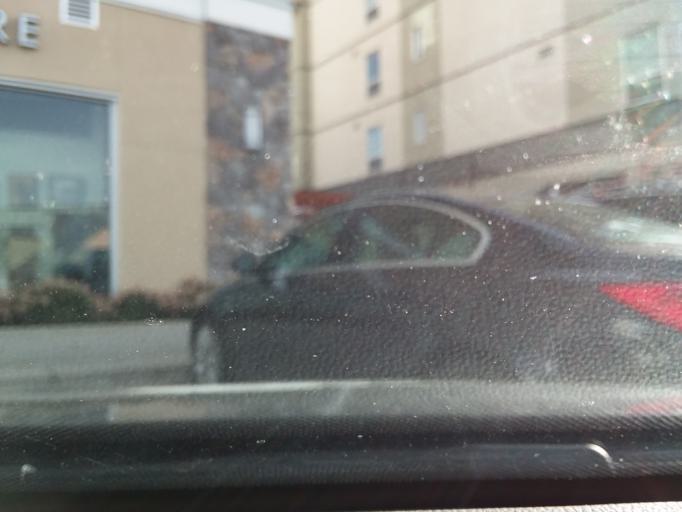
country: CA
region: British Columbia
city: Colwood
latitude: 48.4458
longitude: -123.4695
